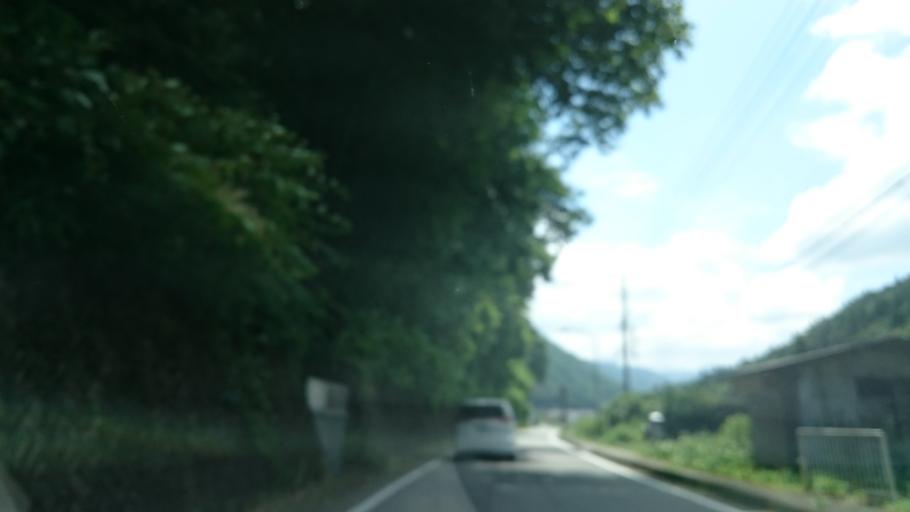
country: JP
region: Gifu
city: Takayama
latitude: 35.9301
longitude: 137.3047
